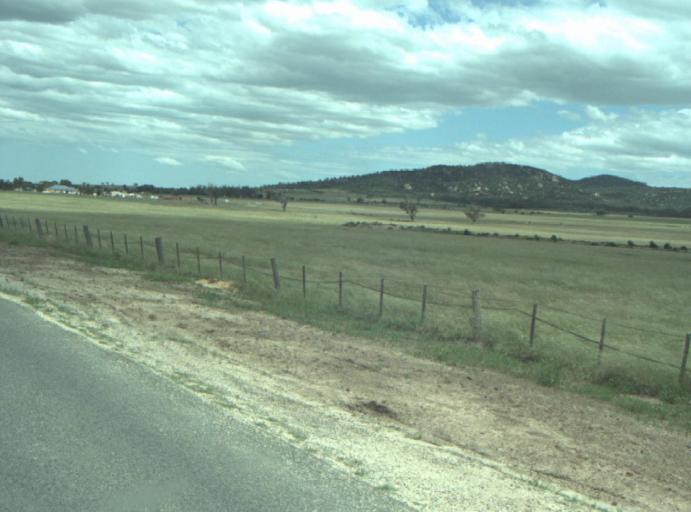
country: AU
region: Victoria
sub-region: Wyndham
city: Little River
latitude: -37.9131
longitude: 144.4624
